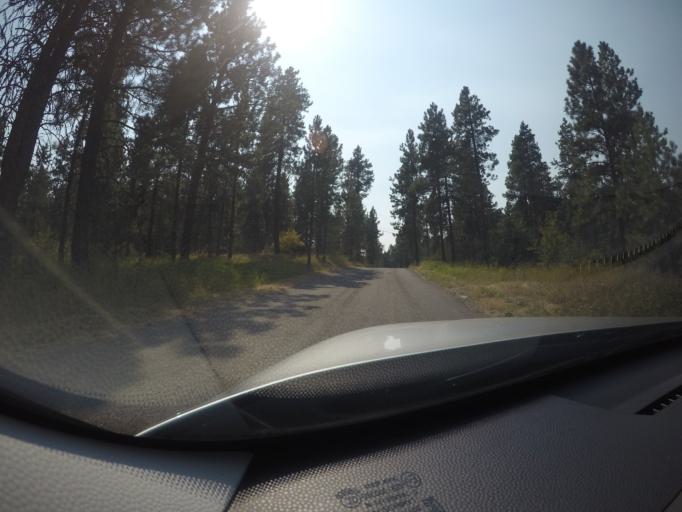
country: US
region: Montana
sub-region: Lake County
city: Polson
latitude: 47.7639
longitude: -114.1582
